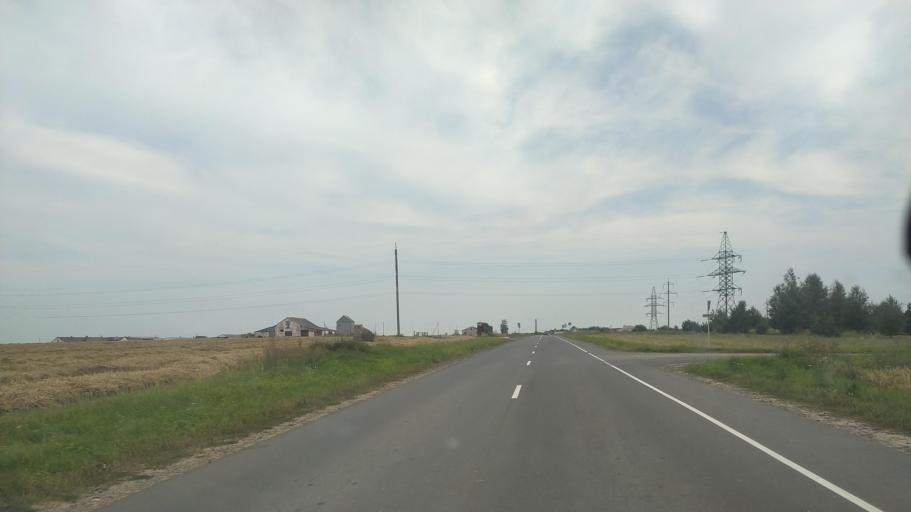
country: BY
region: Brest
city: Byaroza
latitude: 52.5498
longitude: 24.9560
